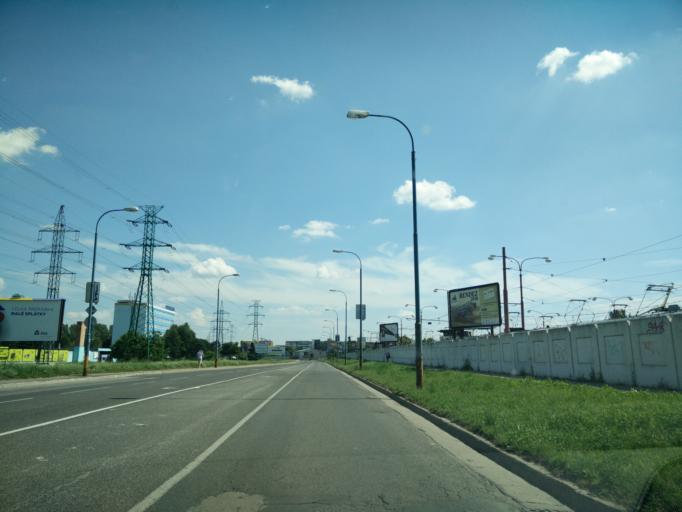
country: SK
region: Bratislavsky
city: Bratislava
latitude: 48.1814
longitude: 17.1639
